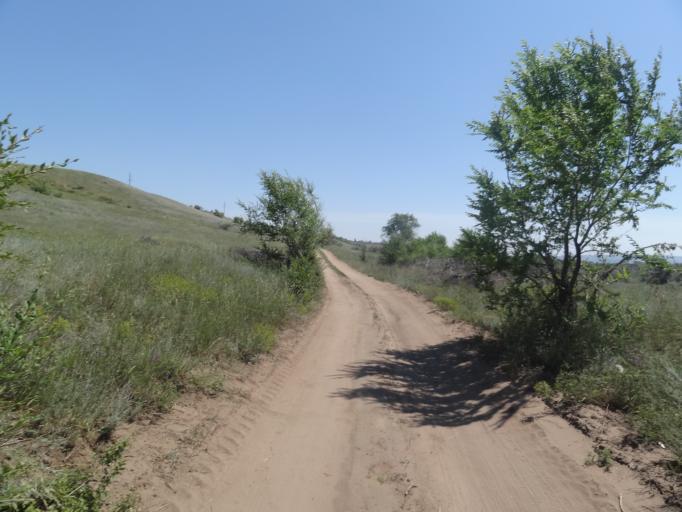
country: RU
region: Saratov
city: Krasnoarmeysk
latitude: 51.1378
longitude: 45.9341
